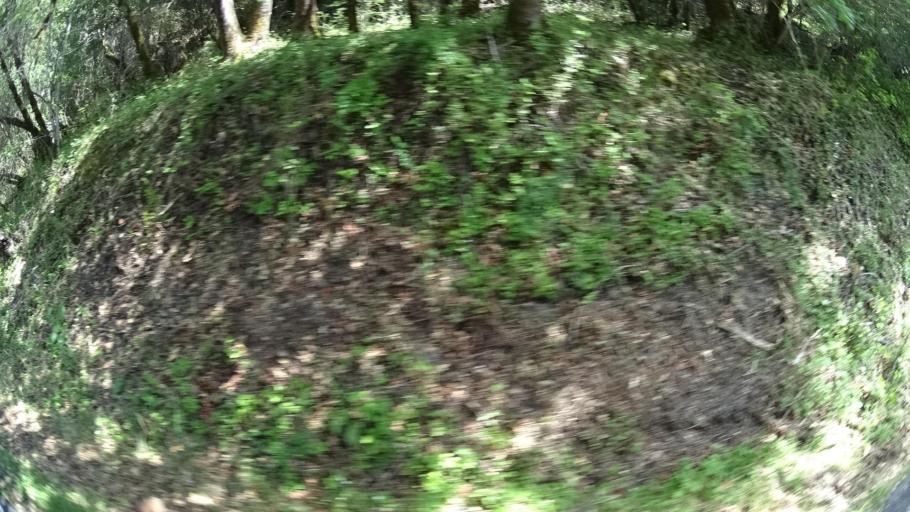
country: US
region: California
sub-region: Humboldt County
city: Redway
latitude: 40.2719
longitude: -123.6255
